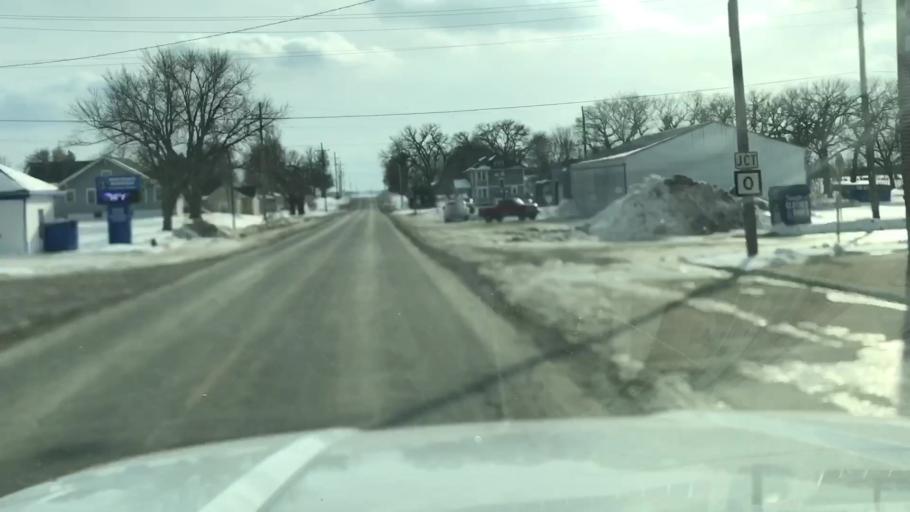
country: US
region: Missouri
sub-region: Gentry County
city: Stanberry
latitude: 40.3514
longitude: -94.6733
